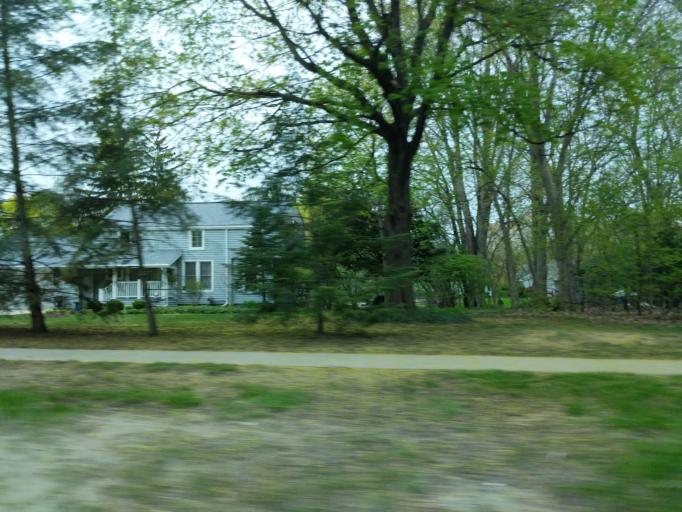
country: US
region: Michigan
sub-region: Midland County
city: Midland
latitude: 43.6327
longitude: -84.2270
